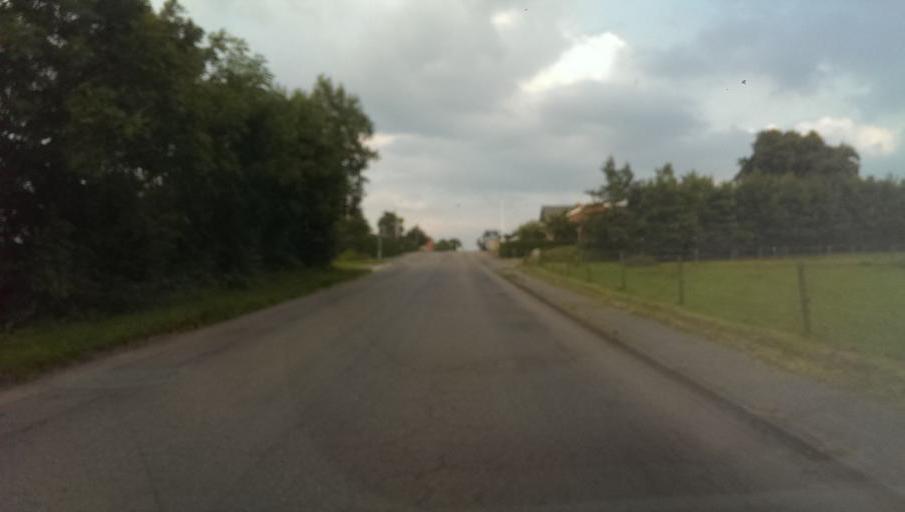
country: DK
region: South Denmark
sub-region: Esbjerg Kommune
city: Tjaereborg
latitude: 55.5521
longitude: 8.6326
